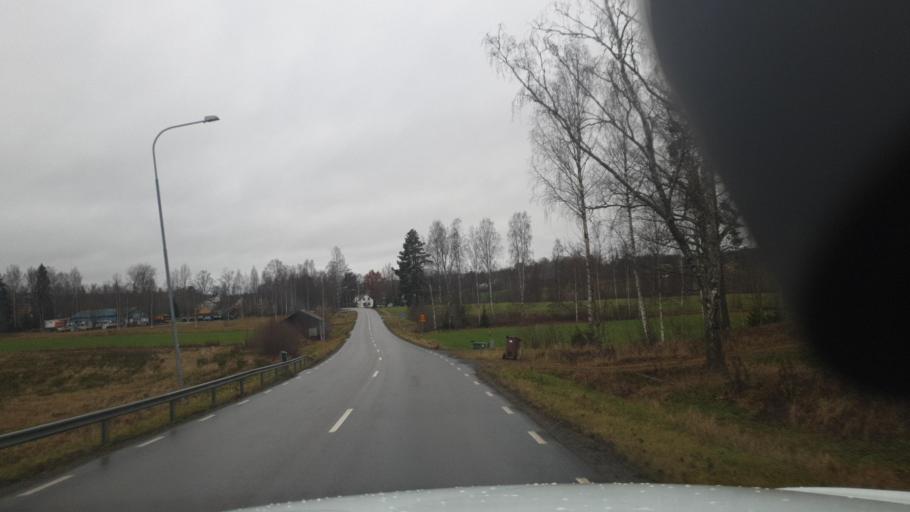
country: SE
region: Vaermland
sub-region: Arvika Kommun
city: Arvika
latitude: 59.5458
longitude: 12.5714
